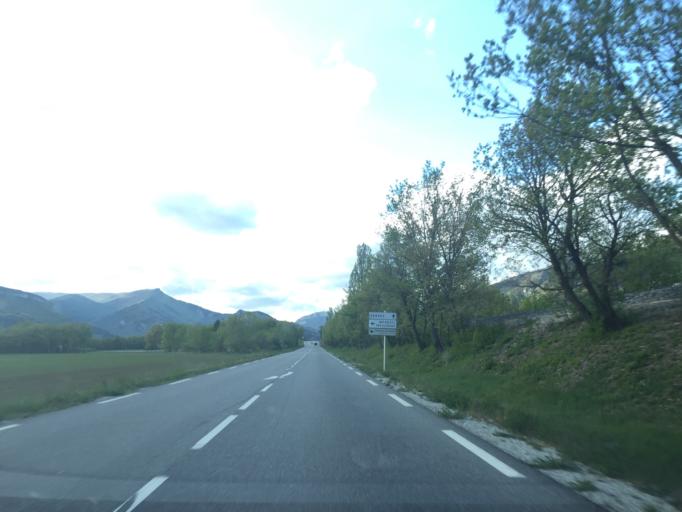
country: FR
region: Provence-Alpes-Cote d'Azur
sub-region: Departement des Hautes-Alpes
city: Serres
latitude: 44.3921
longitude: 5.7399
